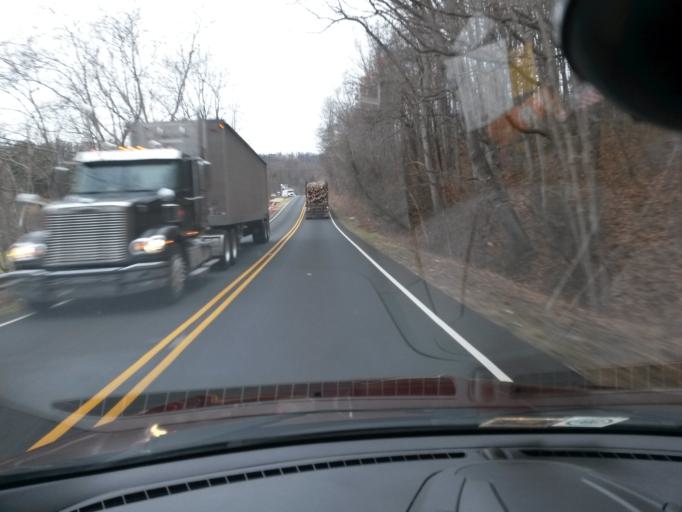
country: US
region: Virginia
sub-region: Amherst County
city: Amherst
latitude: 37.6640
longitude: -79.1615
